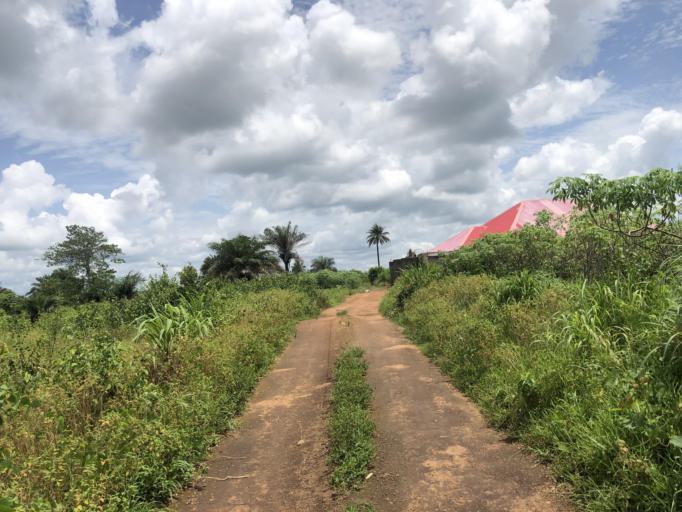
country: SL
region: Northern Province
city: Magburaka
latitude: 8.7003
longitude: -11.9248
